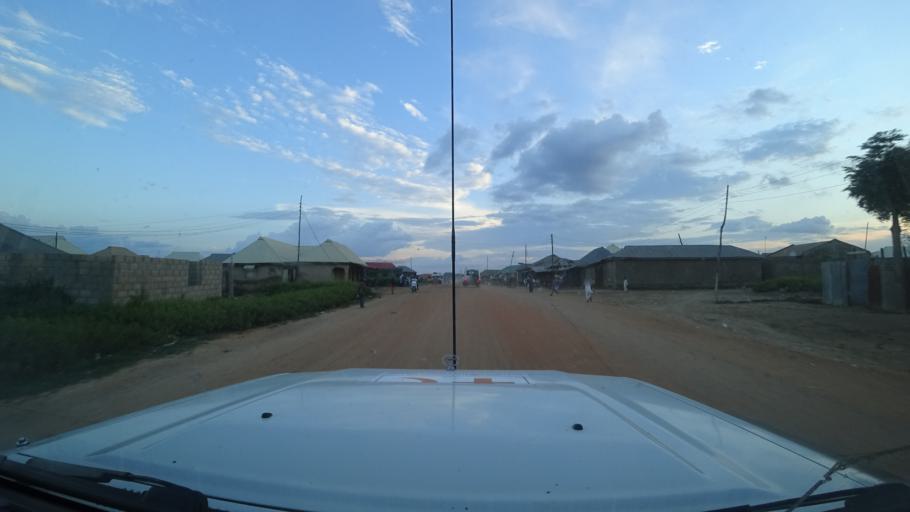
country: NG
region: Niger
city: Minna
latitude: 9.6437
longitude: 6.5806
